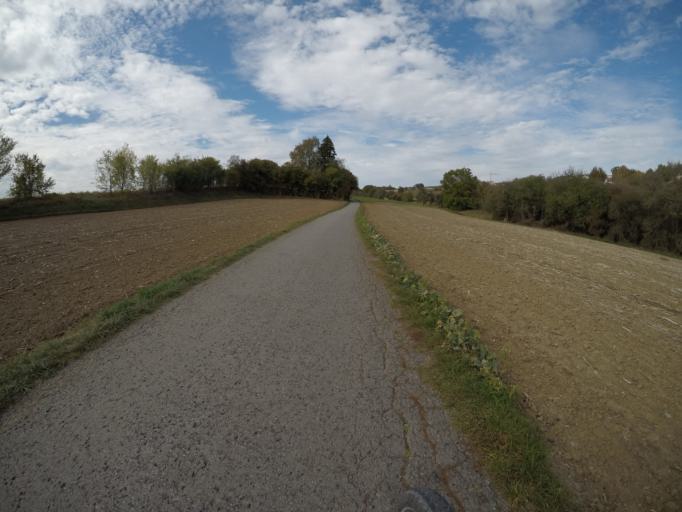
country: DE
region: Baden-Wuerttemberg
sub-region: Regierungsbezirk Stuttgart
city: Herrenberg
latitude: 48.5907
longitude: 8.8503
